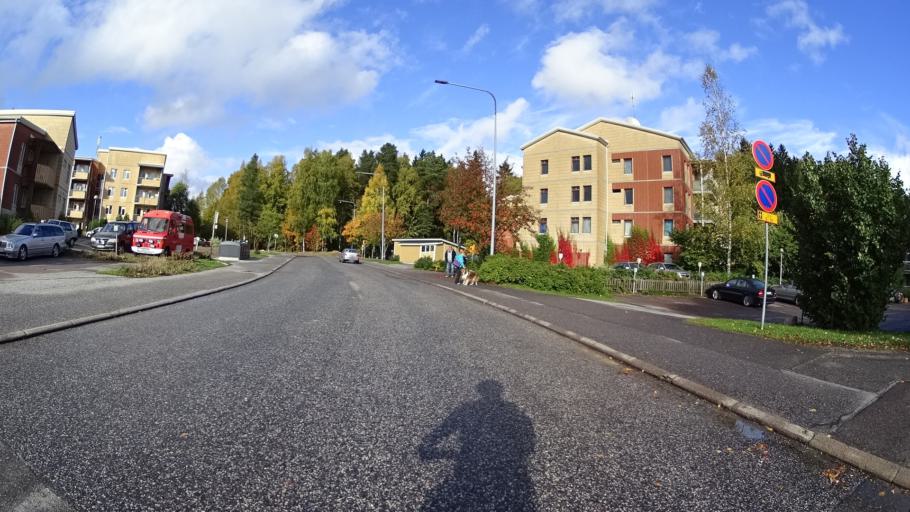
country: FI
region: Uusimaa
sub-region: Helsinki
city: Kilo
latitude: 60.2571
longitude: 24.8005
